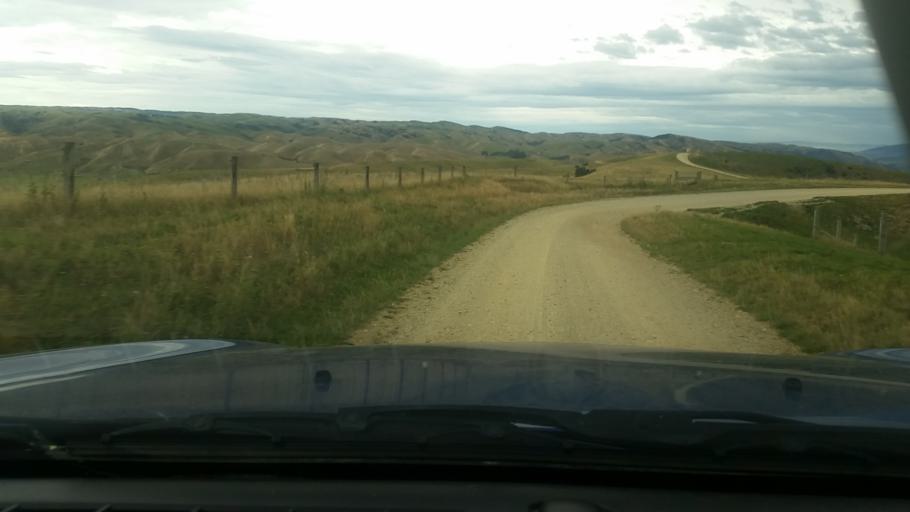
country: NZ
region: Otago
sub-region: Clutha District
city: Balclutha
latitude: -45.7092
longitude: 169.5277
